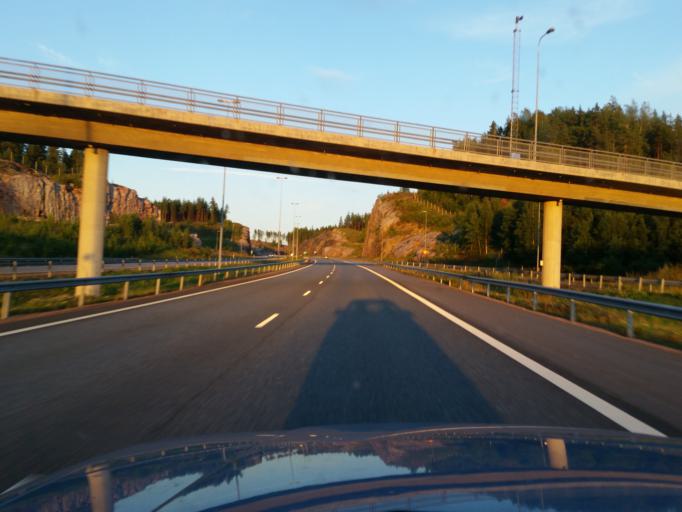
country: FI
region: Varsinais-Suomi
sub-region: Salo
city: Muurla
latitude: 60.3796
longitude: 23.3196
